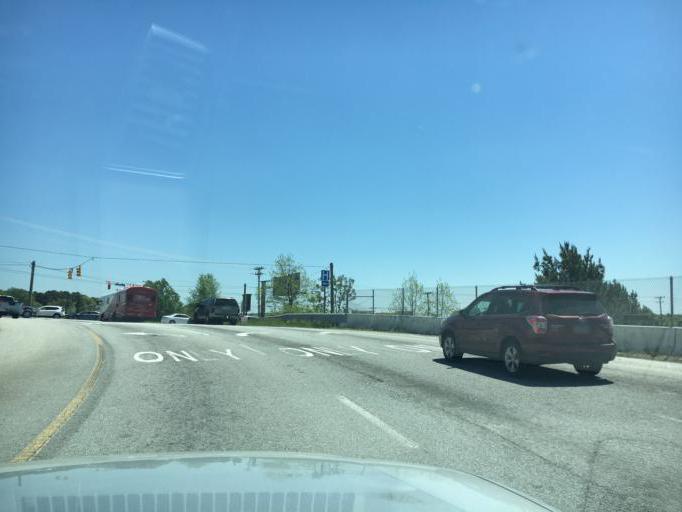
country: US
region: South Carolina
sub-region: Greenville County
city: Simpsonville
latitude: 34.7183
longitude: -82.2563
